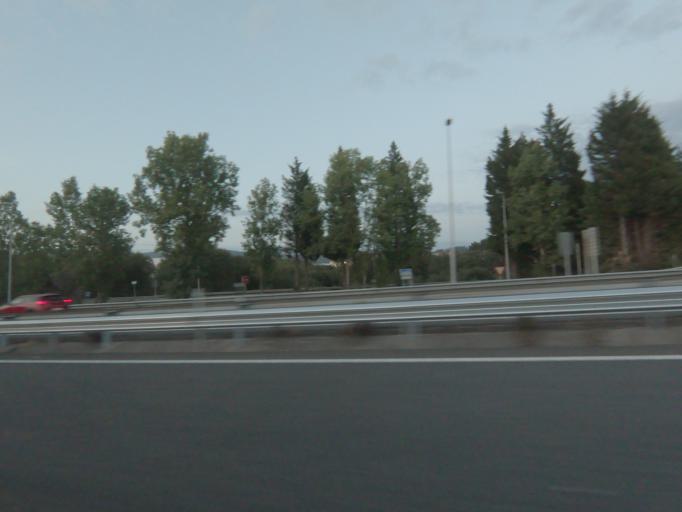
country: ES
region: Galicia
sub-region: Provincia de Pontevedra
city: Porrino
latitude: 42.1040
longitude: -8.6207
